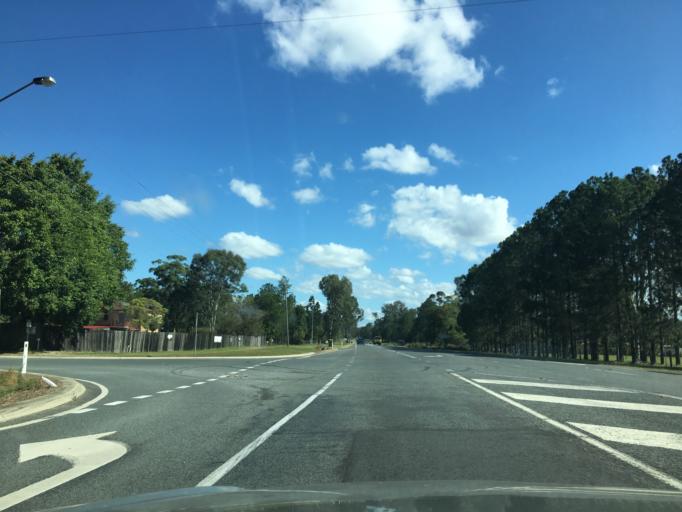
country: AU
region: Queensland
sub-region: Logan
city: Waterford West
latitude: -27.7157
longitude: 153.1291
